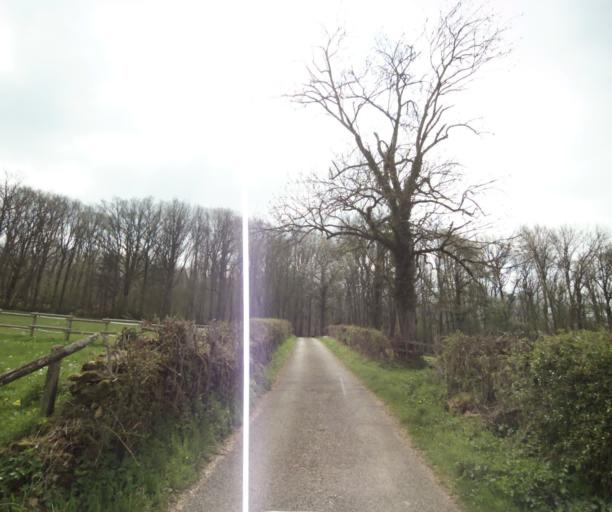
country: FR
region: Bourgogne
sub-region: Departement de Saone-et-Loire
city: Charolles
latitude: 46.3905
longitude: 4.2717
